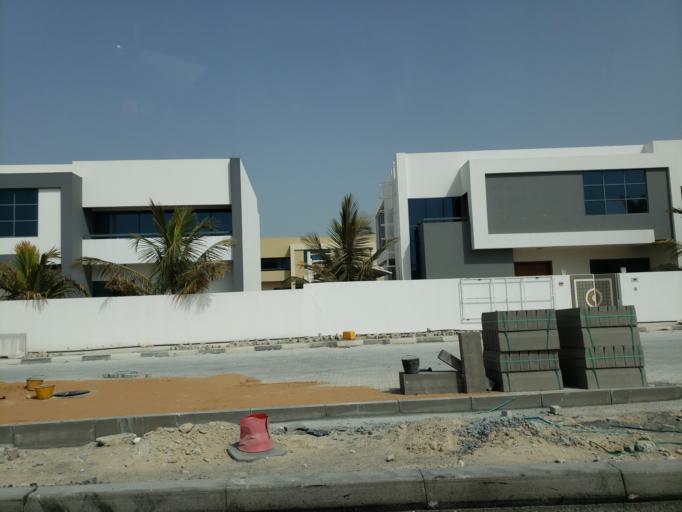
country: AE
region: Ajman
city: Ajman
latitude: 25.4205
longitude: 55.4904
